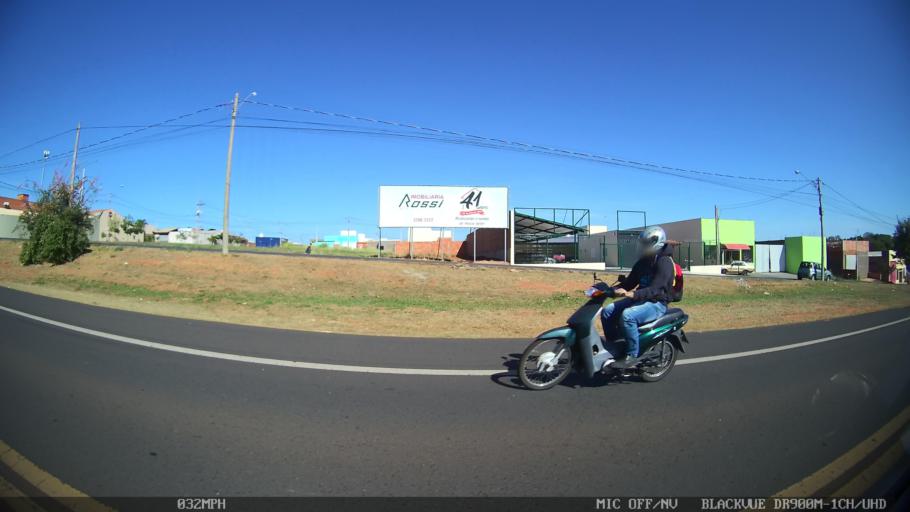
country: BR
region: Sao Paulo
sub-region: Olimpia
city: Olimpia
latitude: -20.7379
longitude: -48.8840
